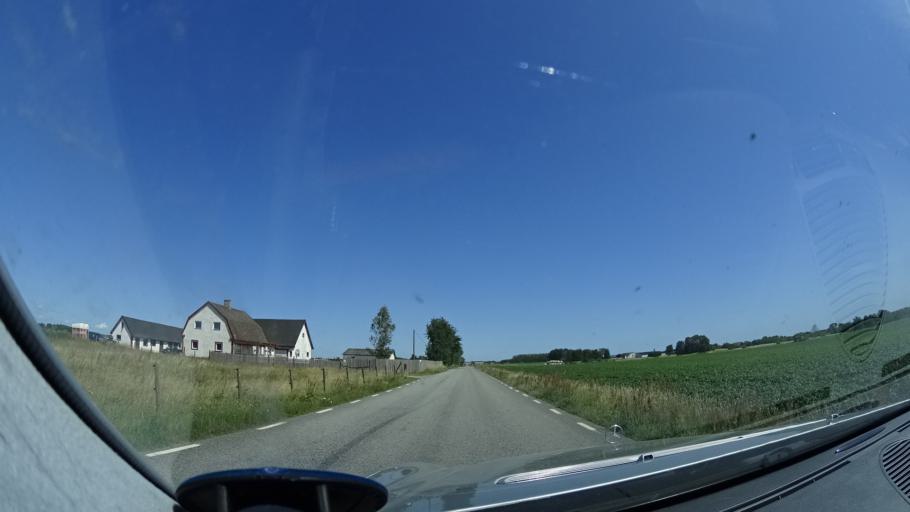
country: SE
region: Skane
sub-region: Kristianstads Kommun
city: Degeberga
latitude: 55.8864
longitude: 14.0261
